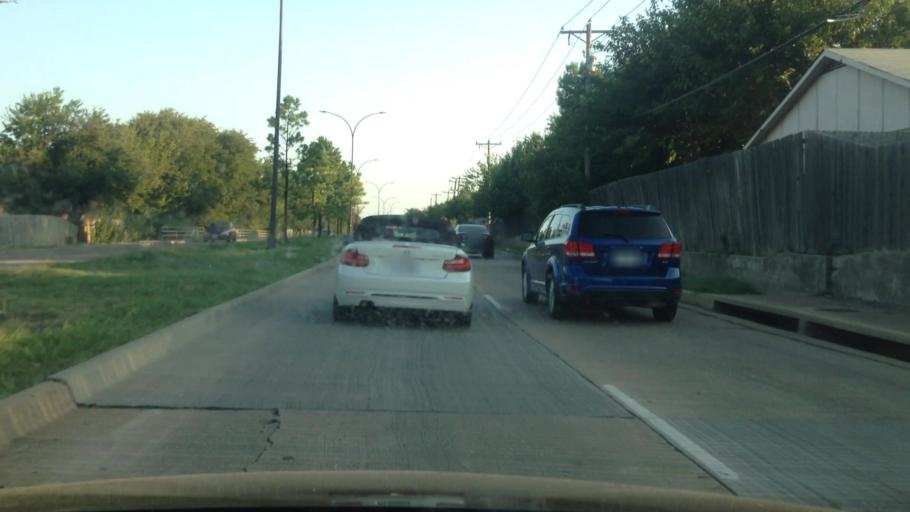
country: US
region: Texas
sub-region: Tarrant County
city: Dalworthington Gardens
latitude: 32.6656
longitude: -97.1151
